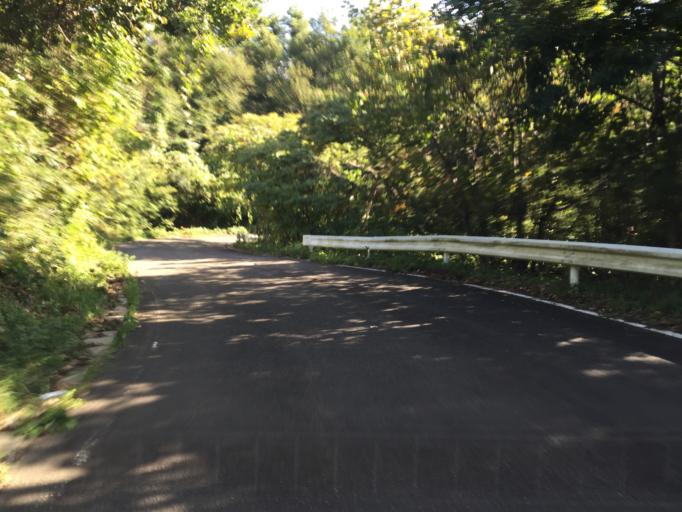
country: JP
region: Fukushima
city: Yanagawamachi-saiwaicho
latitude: 37.8344
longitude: 140.7001
